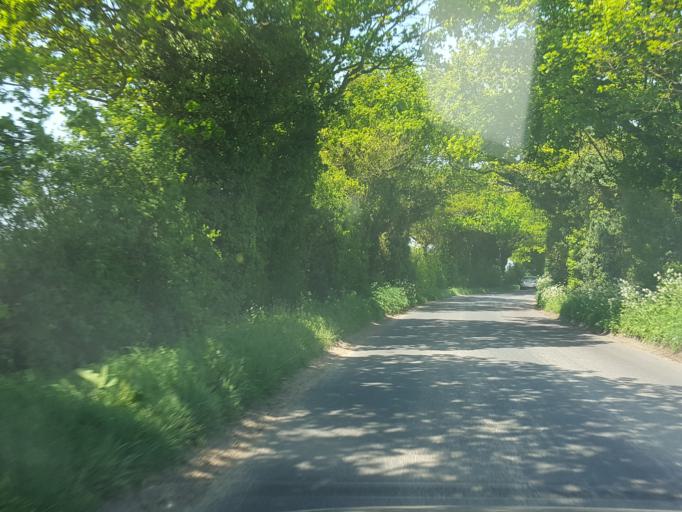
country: GB
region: England
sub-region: Essex
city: Great Bentley
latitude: 51.8551
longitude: 1.0400
